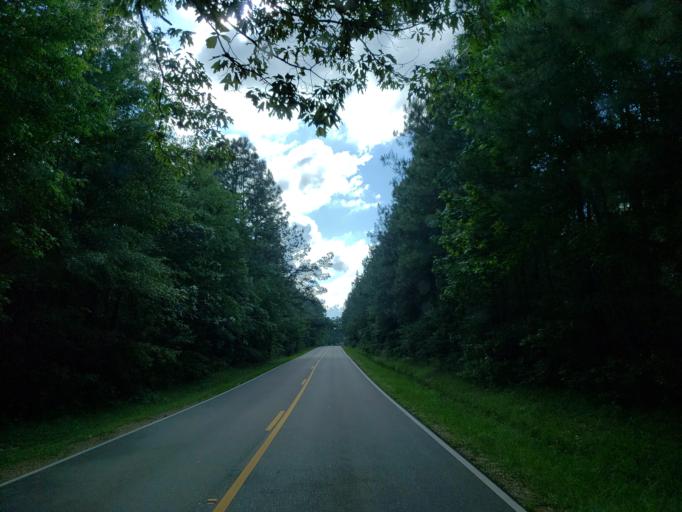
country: US
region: Mississippi
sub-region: Lamar County
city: Sumrall
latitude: 31.3546
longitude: -89.4946
